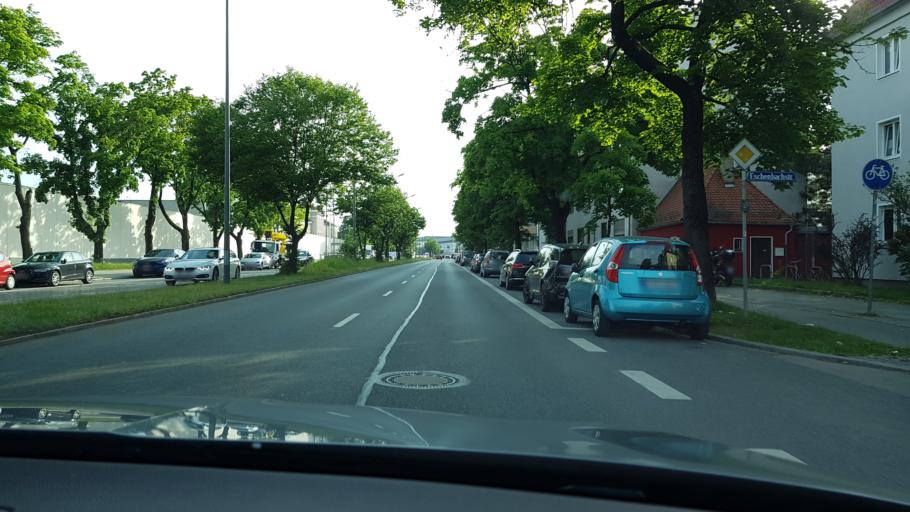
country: DE
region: Bavaria
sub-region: Upper Bavaria
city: Munich
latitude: 48.1019
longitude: 11.5935
